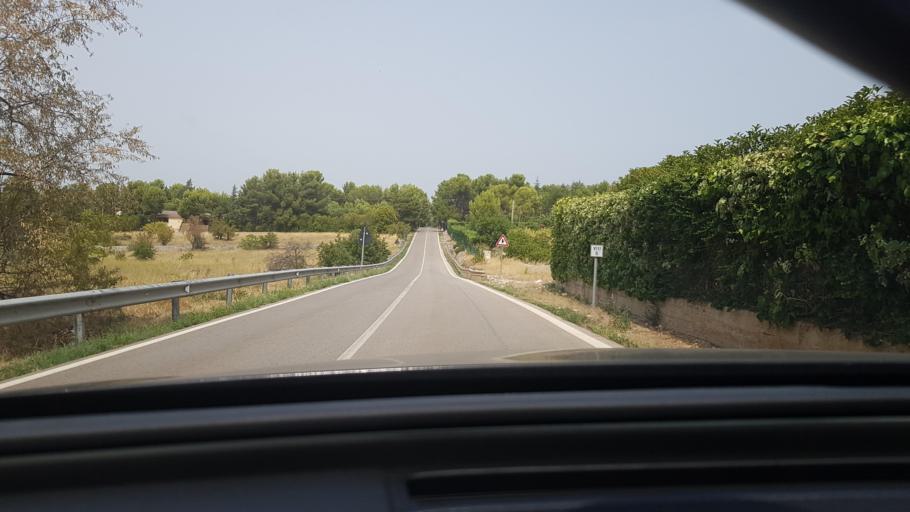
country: IT
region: Apulia
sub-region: Provincia di Barletta - Andria - Trani
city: Andria
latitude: 41.1235
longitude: 16.2869
